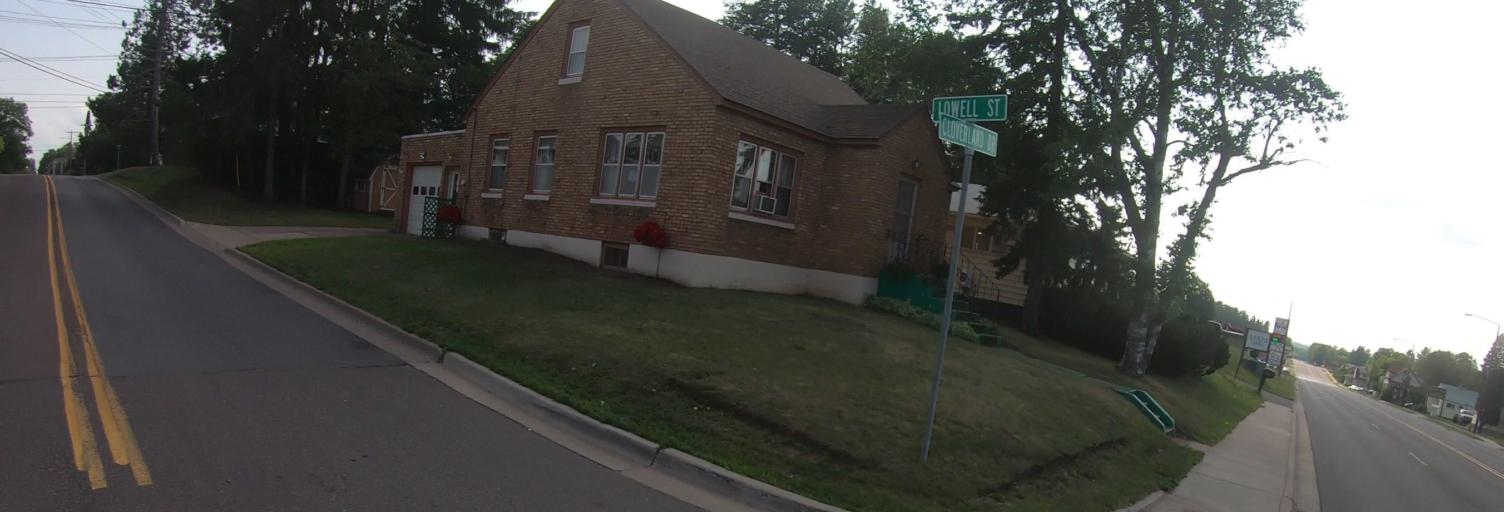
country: US
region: Michigan
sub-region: Gogebic County
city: Ironwood
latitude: 46.4632
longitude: -90.1727
